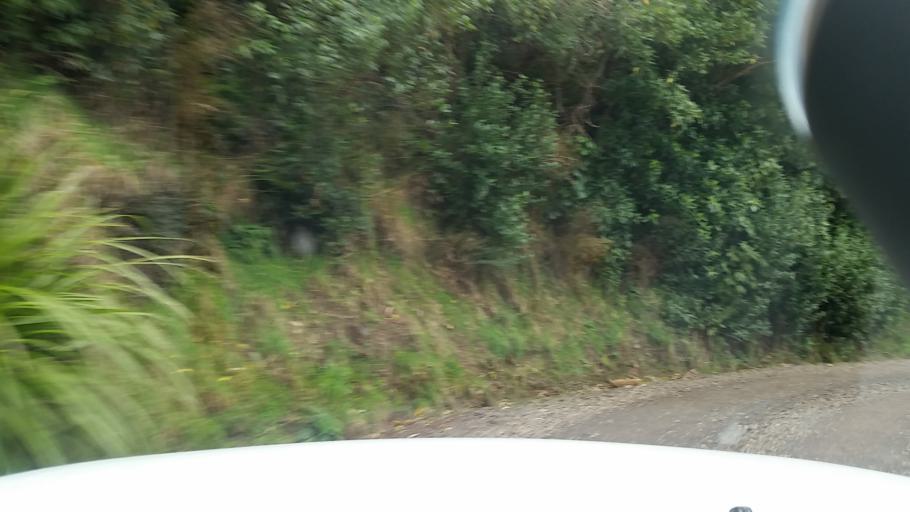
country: NZ
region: Canterbury
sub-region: Christchurch City
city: Christchurch
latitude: -43.7220
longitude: 172.7986
